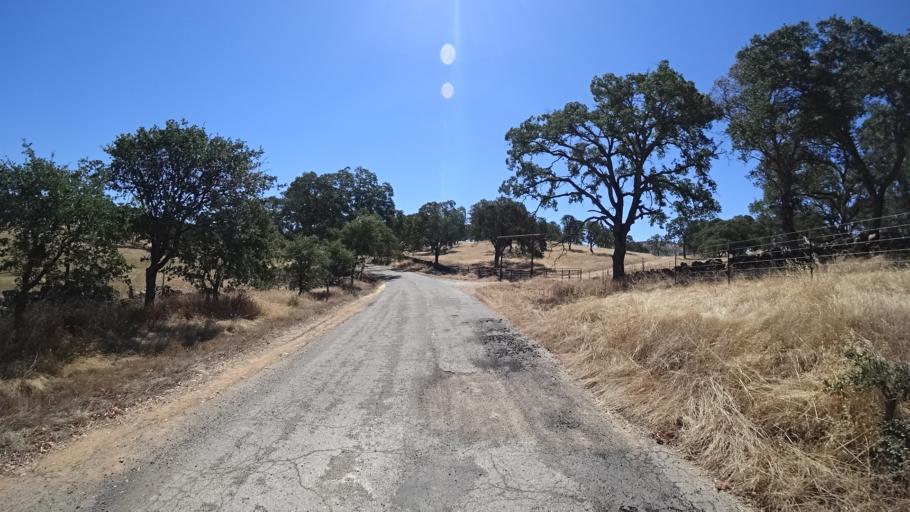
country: US
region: California
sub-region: Calaveras County
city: Copperopolis
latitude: 37.9346
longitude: -120.7403
